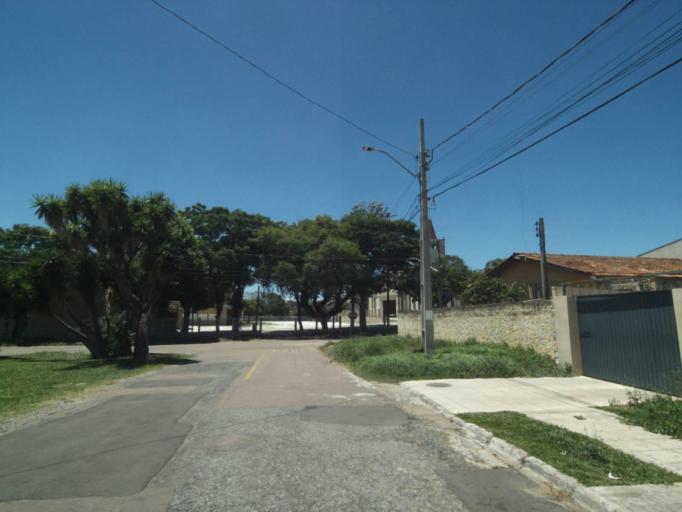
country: BR
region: Parana
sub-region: Curitiba
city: Curitiba
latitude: -25.4858
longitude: -49.3453
